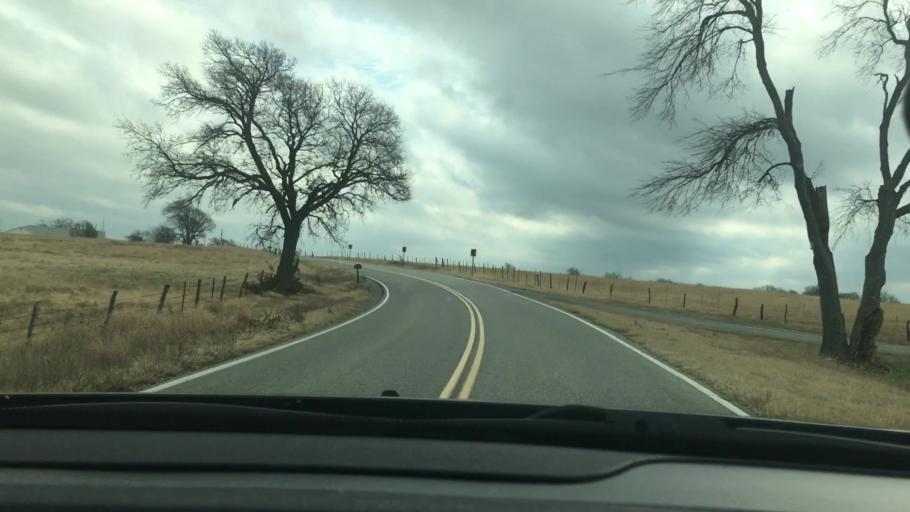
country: US
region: Oklahoma
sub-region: Bryan County
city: Durant
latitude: 34.0890
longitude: -96.4835
